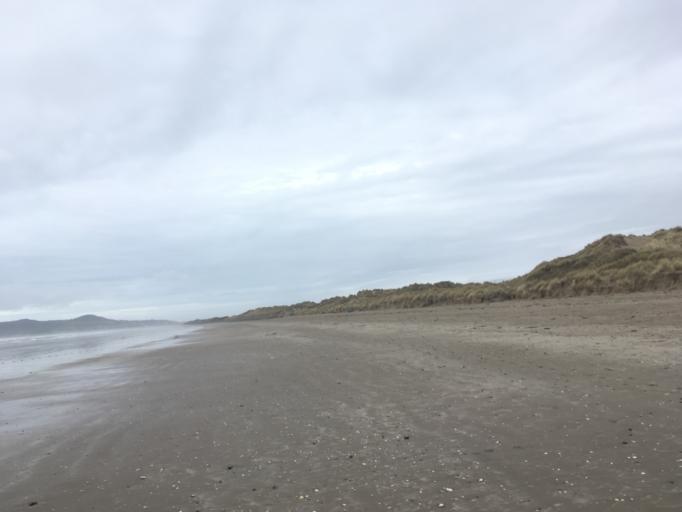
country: IE
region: Leinster
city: Portmarnock
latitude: 53.4211
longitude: -6.1214
